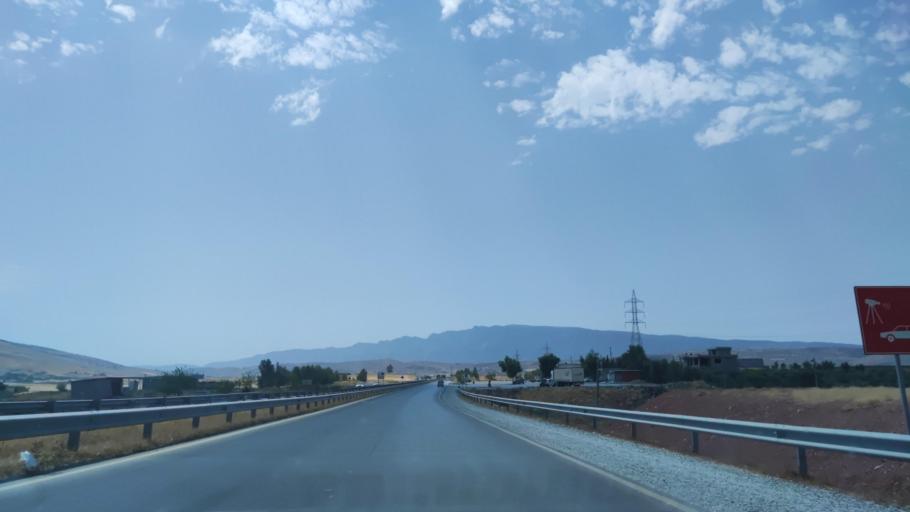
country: IQ
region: Arbil
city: Shaqlawah
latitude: 36.4850
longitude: 44.3812
